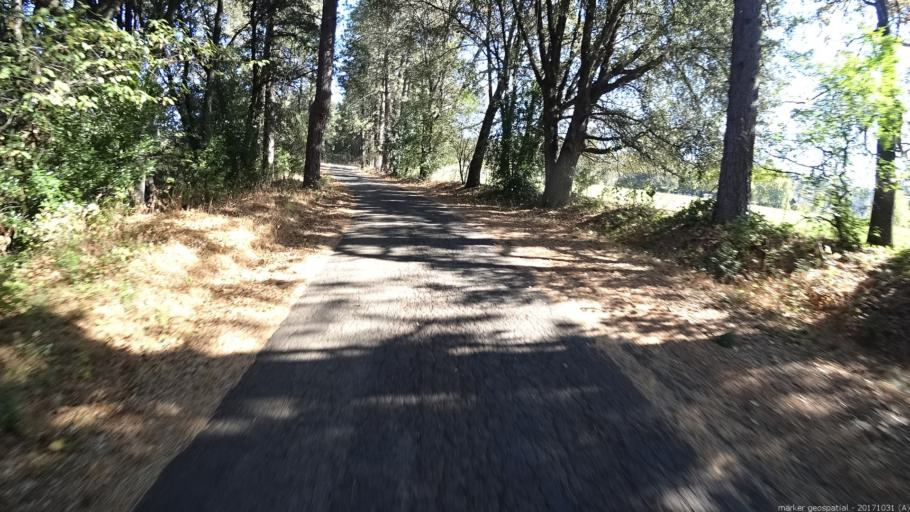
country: US
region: California
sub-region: Shasta County
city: Shingletown
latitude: 40.5306
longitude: -121.9517
